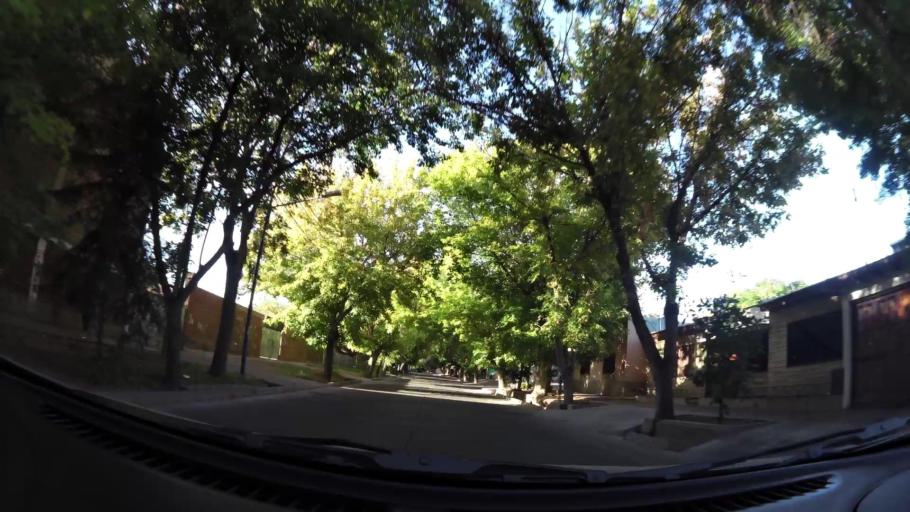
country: AR
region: Mendoza
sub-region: Departamento de Godoy Cruz
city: Godoy Cruz
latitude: -32.9445
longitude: -68.8497
